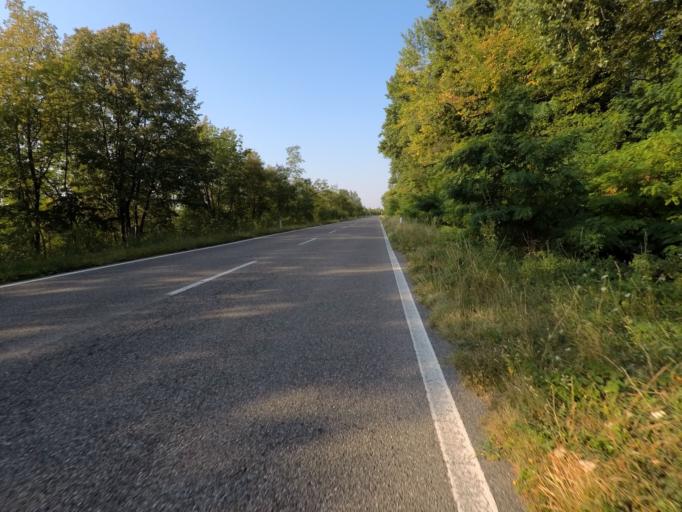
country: IT
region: Friuli Venezia Giulia
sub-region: Provincia di Udine
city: Trasaghis
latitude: 46.2728
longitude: 13.0573
